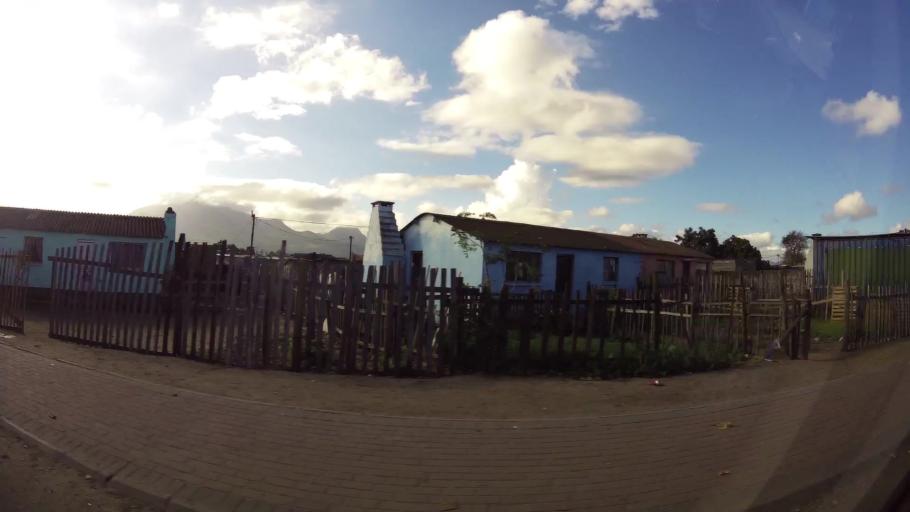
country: ZA
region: Western Cape
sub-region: Eden District Municipality
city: George
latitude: -33.9849
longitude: 22.4776
